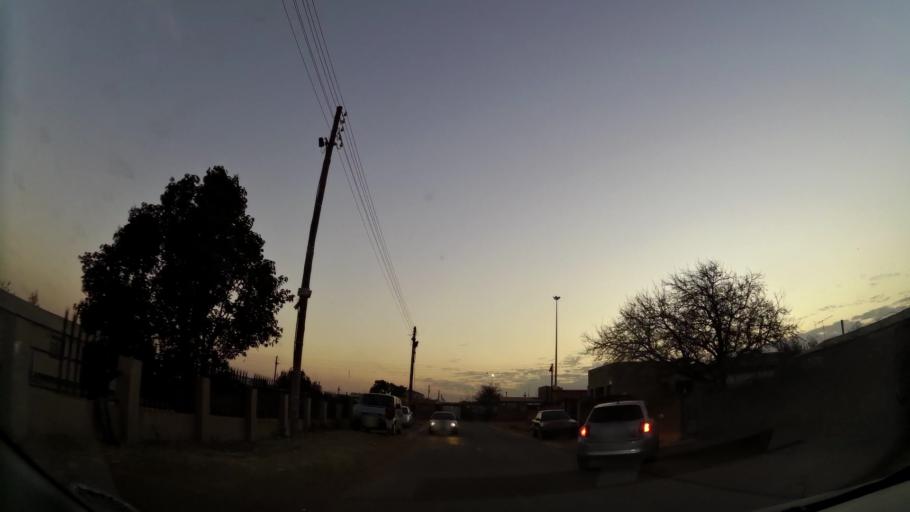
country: ZA
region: Gauteng
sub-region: West Rand District Municipality
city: Randfontein
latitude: -26.2079
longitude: 27.7118
